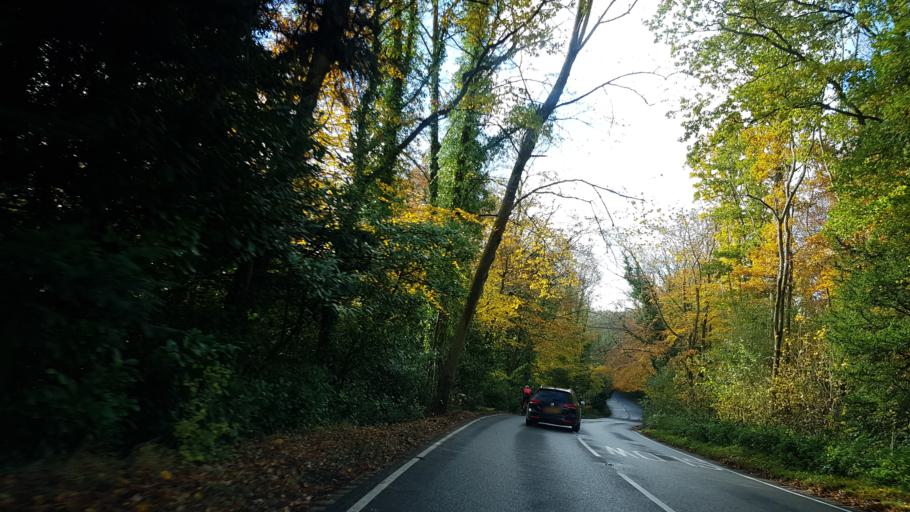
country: GB
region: England
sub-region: Surrey
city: Haslemere
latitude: 51.1076
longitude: -0.6880
